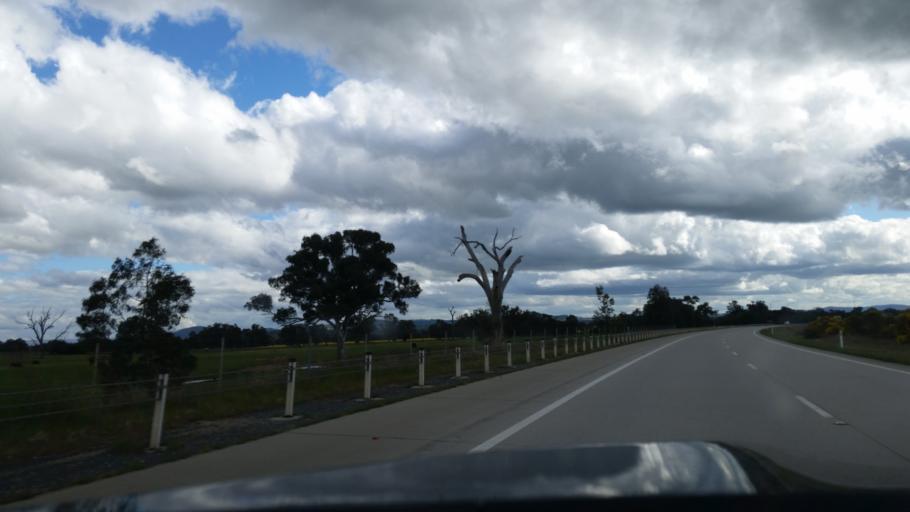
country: AU
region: New South Wales
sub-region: Albury Municipality
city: Lavington
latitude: -35.9273
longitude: 147.0826
